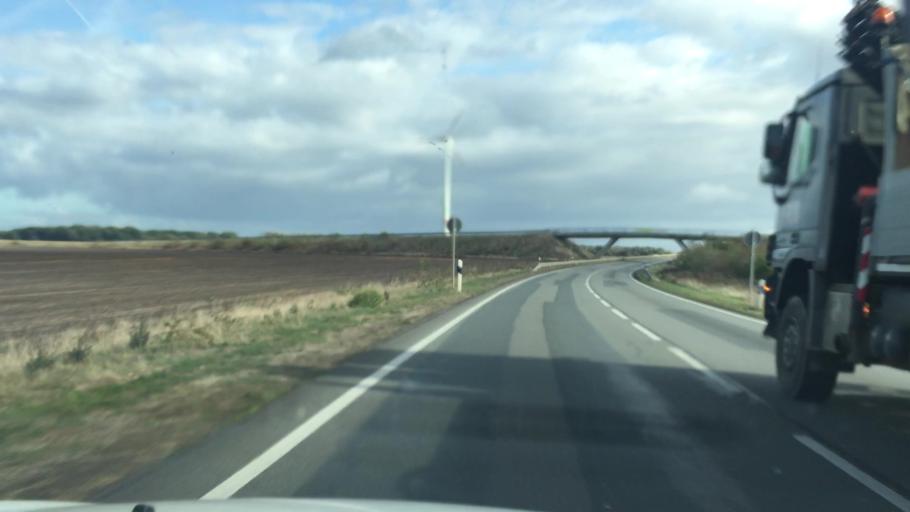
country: DE
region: Lower Saxony
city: Diepholz
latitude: 52.6275
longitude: 8.4025
